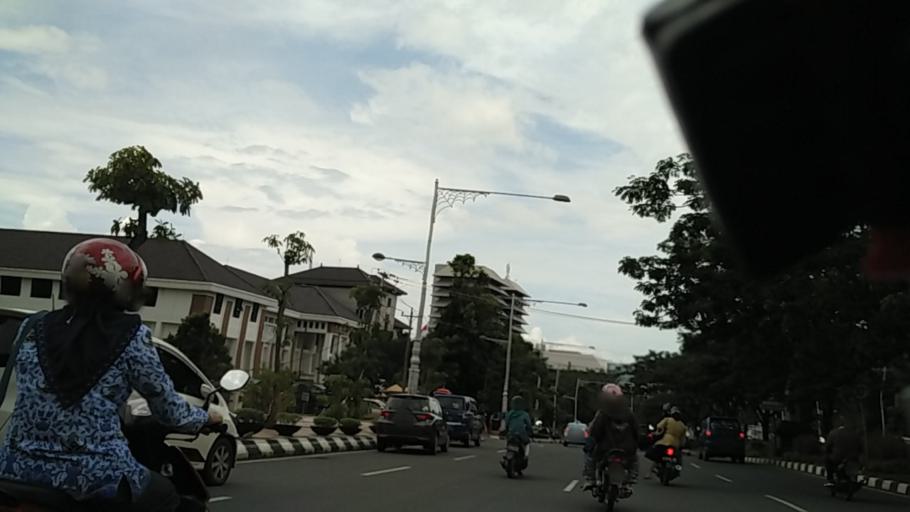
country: ID
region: Central Java
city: Semarang
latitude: -6.9971
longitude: 110.4194
